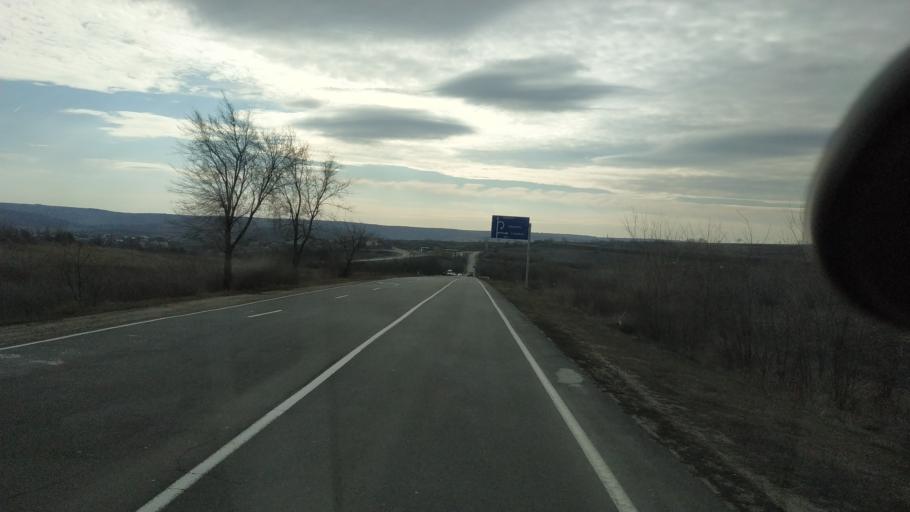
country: MD
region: Chisinau
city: Vadul lui Voda
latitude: 47.0755
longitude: 29.0250
